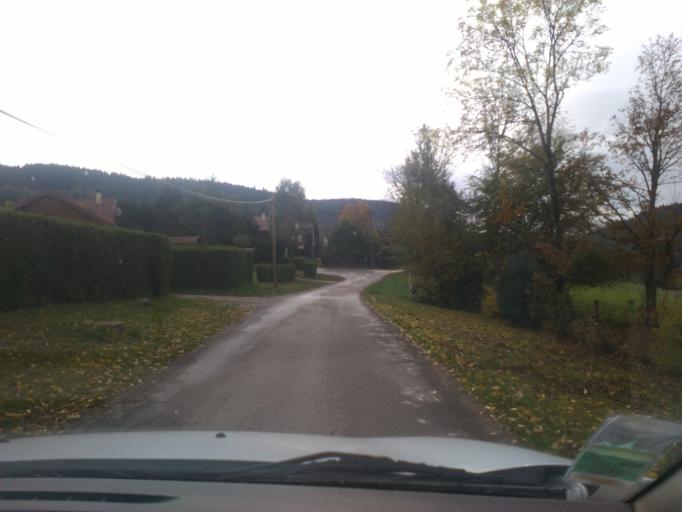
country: FR
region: Lorraine
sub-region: Departement des Vosges
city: Xonrupt-Longemer
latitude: 48.1270
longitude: 6.9083
